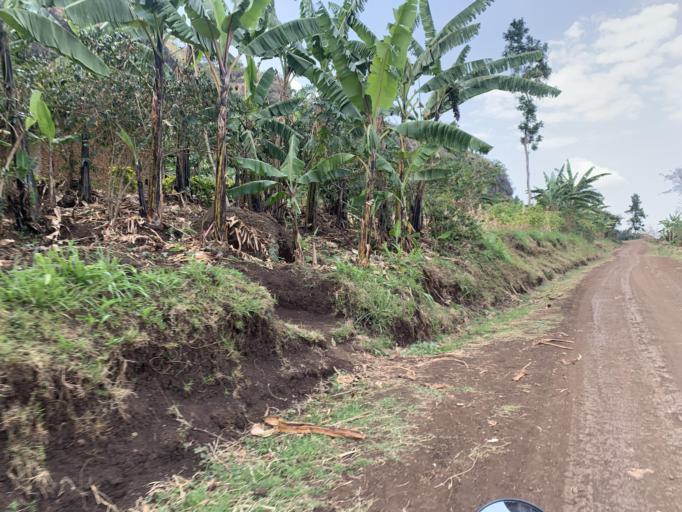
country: UG
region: Eastern Region
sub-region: Sironko District
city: Sironko
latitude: 1.2596
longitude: 34.3062
